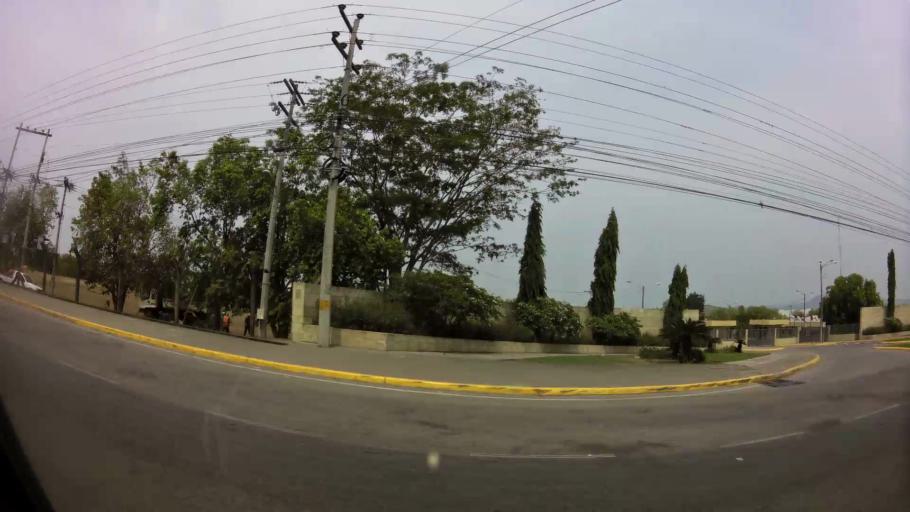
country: HN
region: Cortes
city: Villanueva
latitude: 15.3227
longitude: -87.9918
